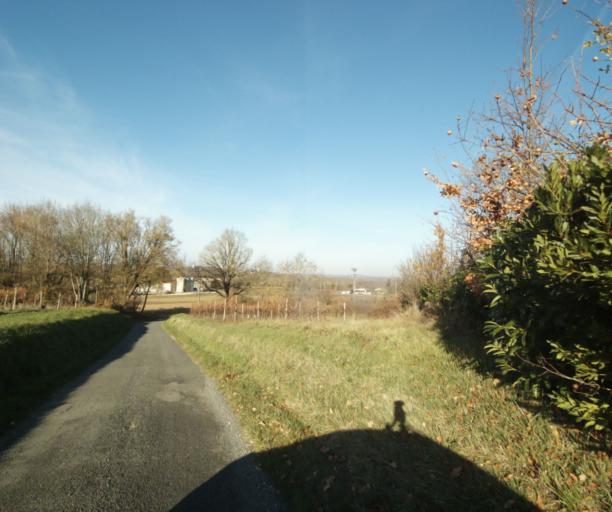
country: FR
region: Poitou-Charentes
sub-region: Departement de la Charente-Maritime
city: Burie
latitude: 45.7814
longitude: -0.4344
